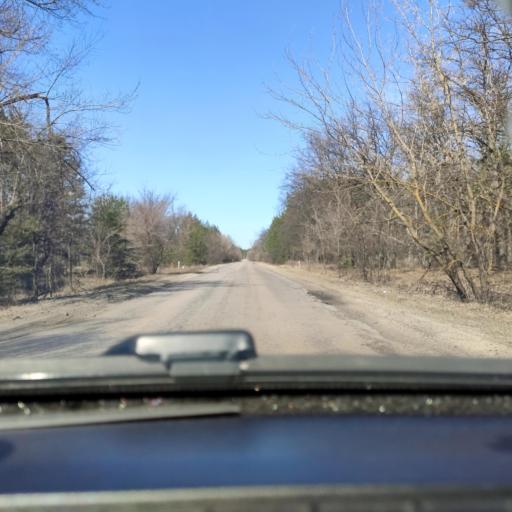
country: RU
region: Voronezj
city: Somovo
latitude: 51.7153
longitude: 39.3668
